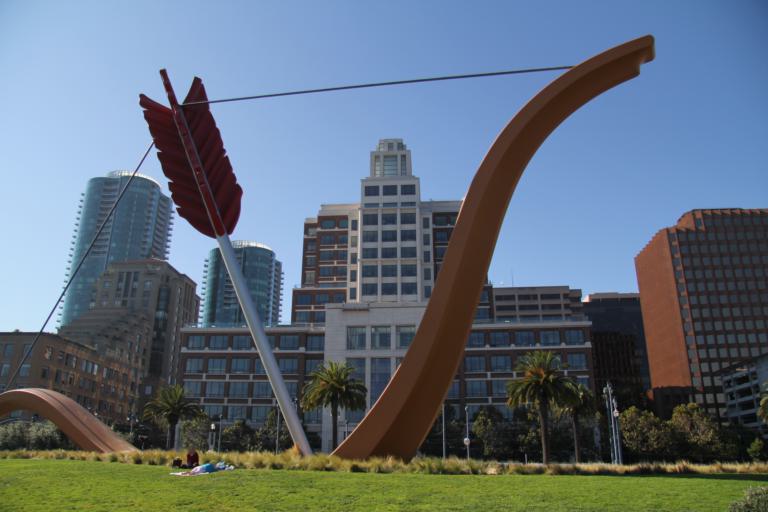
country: US
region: California
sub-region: San Francisco County
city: San Francisco
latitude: 37.7916
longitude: -122.3900
